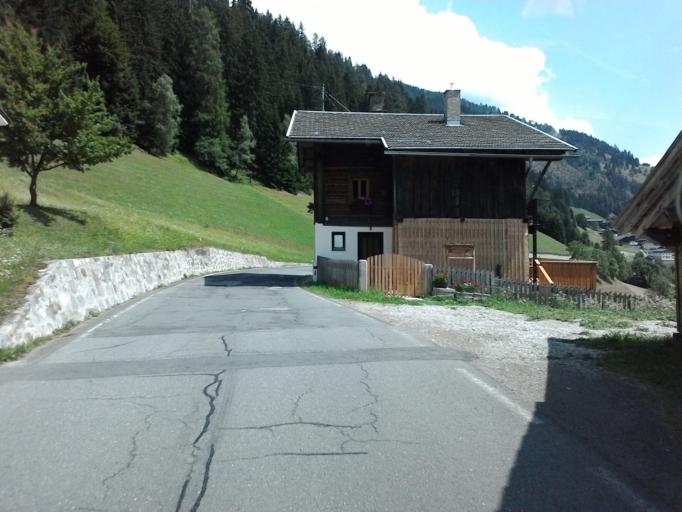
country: AT
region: Tyrol
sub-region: Politischer Bezirk Lienz
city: Untertilliach
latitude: 46.7051
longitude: 12.7226
